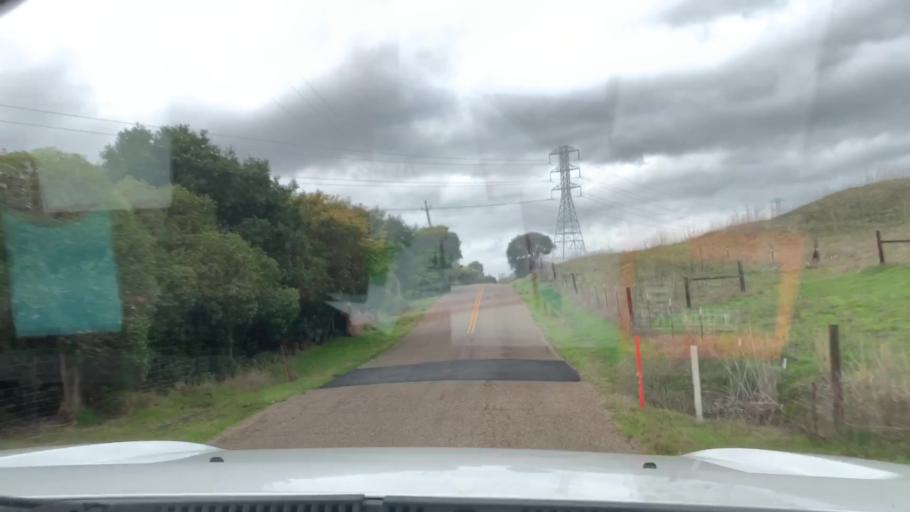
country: US
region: California
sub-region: San Luis Obispo County
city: Morro Bay
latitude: 35.3782
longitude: -120.7878
